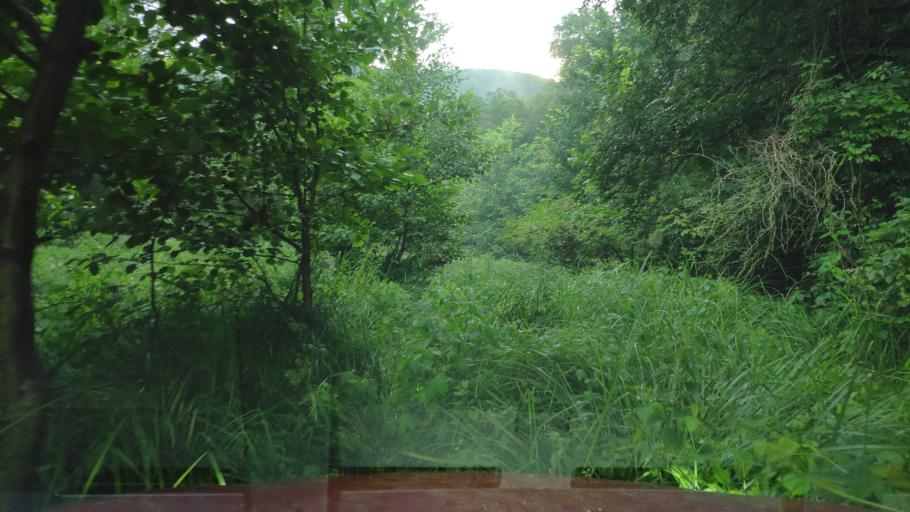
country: SK
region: Presovsky
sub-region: Okres Presov
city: Presov
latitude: 48.8675
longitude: 21.2024
